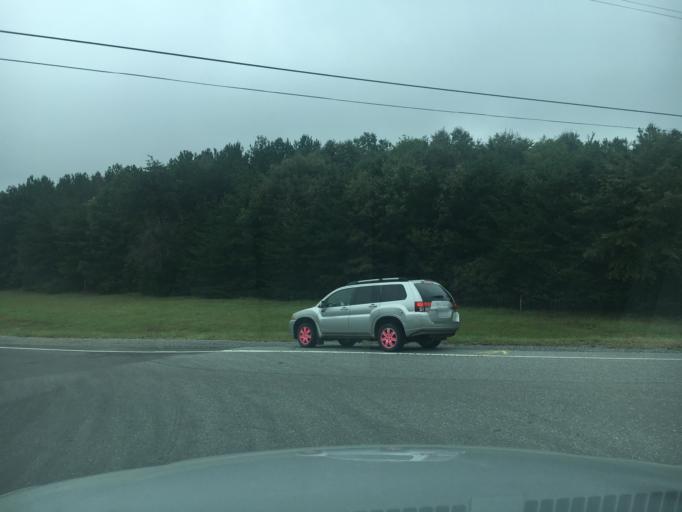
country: US
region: North Carolina
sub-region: Burke County
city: Glen Alpine
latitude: 35.6913
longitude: -81.8409
